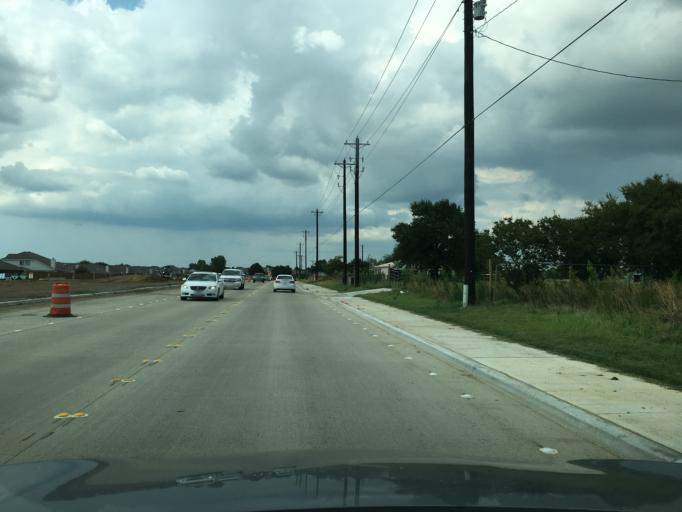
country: US
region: Texas
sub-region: Denton County
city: Oak Point
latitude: 33.1990
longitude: -96.9786
